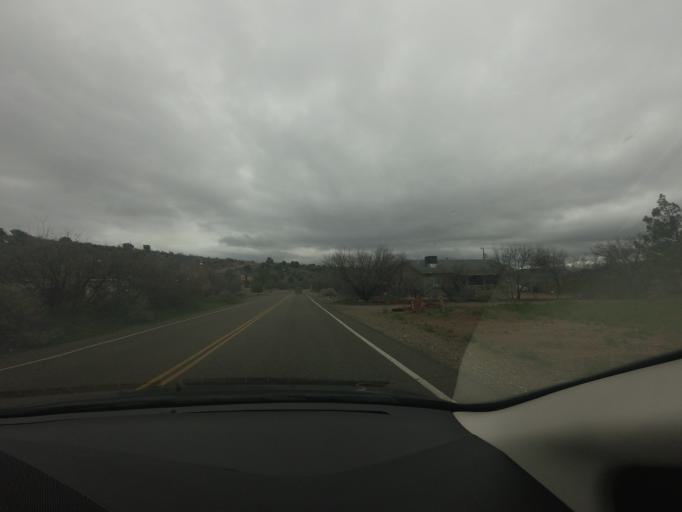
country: US
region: Arizona
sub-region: Yavapai County
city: Lake Montezuma
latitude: 34.6522
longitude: -111.7660
